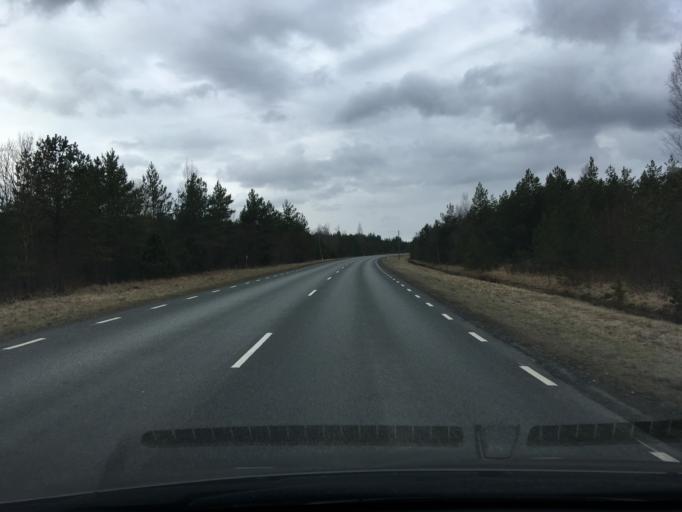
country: EE
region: Laeaene
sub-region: Lihula vald
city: Lihula
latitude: 58.6119
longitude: 23.9247
